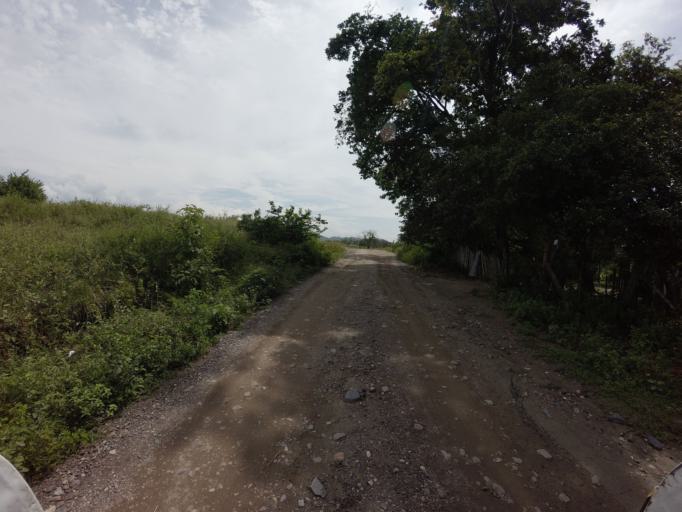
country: CO
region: Tolima
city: Natagaima
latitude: 3.4536
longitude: -75.1441
